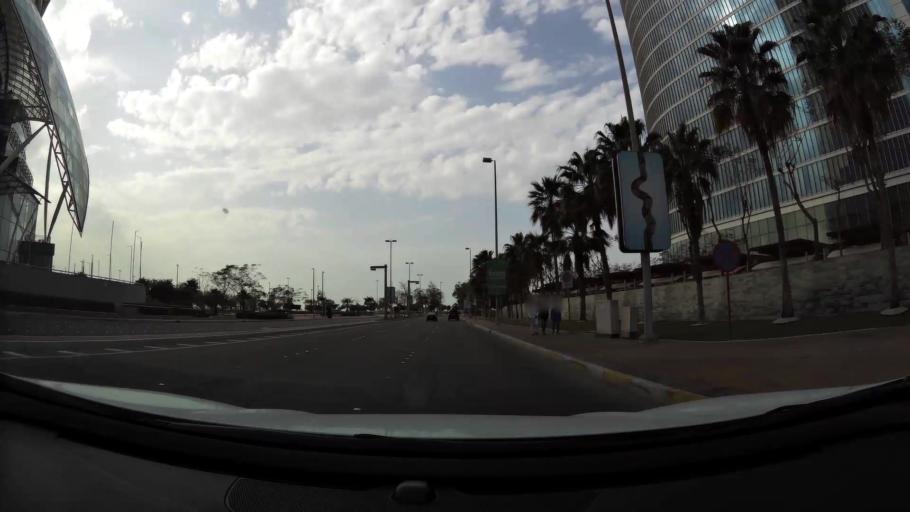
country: AE
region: Abu Dhabi
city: Abu Dhabi
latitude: 24.4855
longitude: 54.3513
